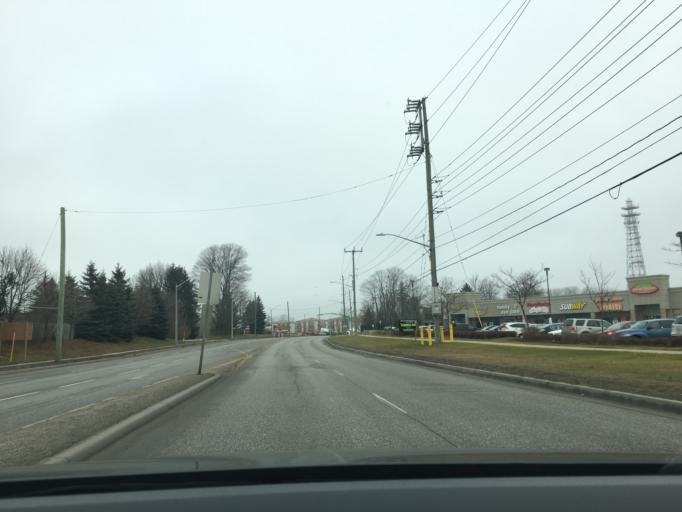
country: CA
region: Ontario
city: Barrie
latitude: 44.3470
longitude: -79.7042
